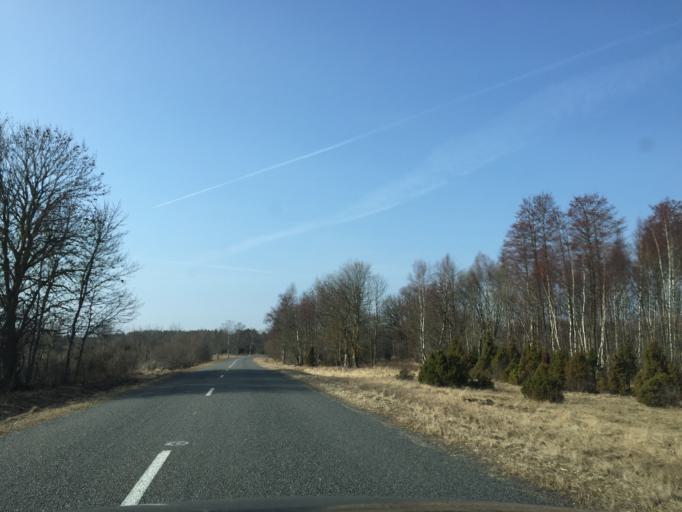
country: LV
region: Dundaga
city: Dundaga
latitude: 57.9191
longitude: 22.0561
